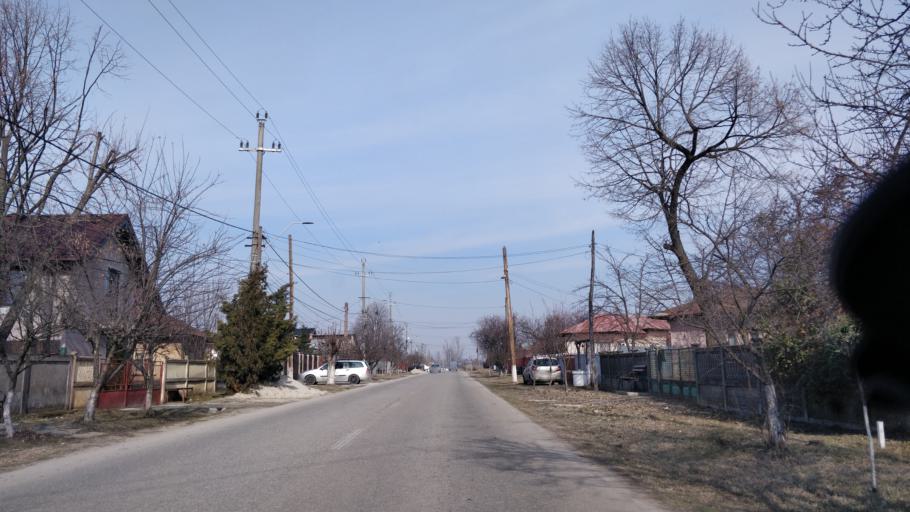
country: RO
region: Giurgiu
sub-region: Comuna Ulmi
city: Ulmi
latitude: 44.4784
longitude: 25.7698
